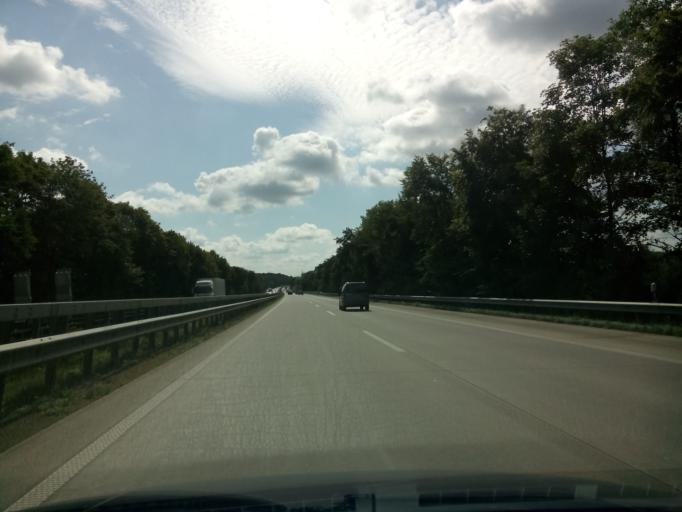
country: DE
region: Lower Saxony
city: Ritterhude
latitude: 53.2020
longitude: 8.6761
